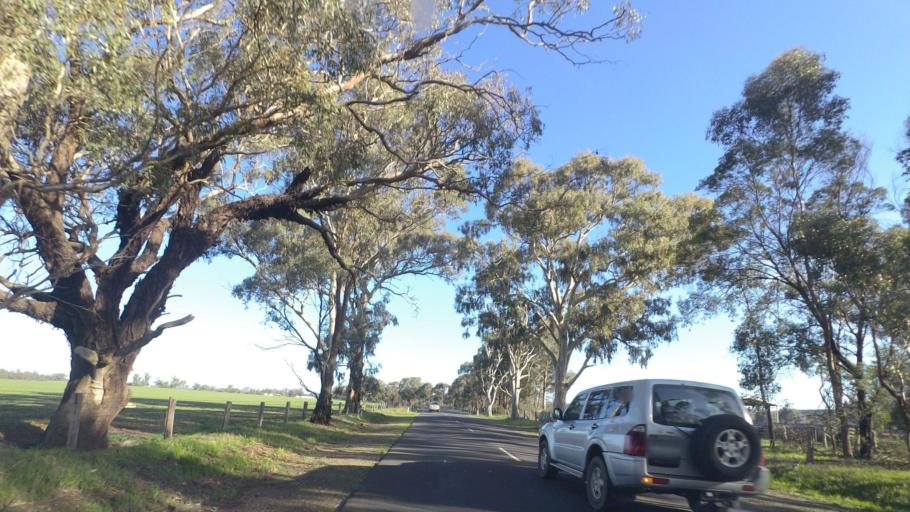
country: AU
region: Victoria
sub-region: Greater Bendigo
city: Epsom
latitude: -36.6841
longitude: 144.5182
